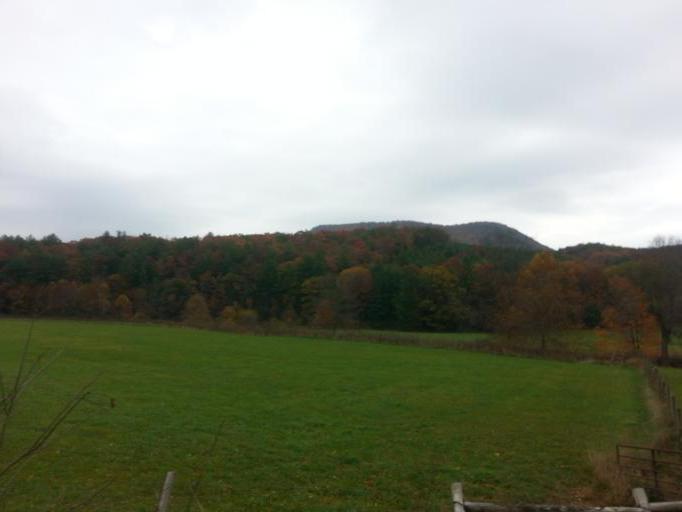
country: US
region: Virginia
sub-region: Pulaski County
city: Pulaski
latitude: 37.1053
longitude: -80.8936
